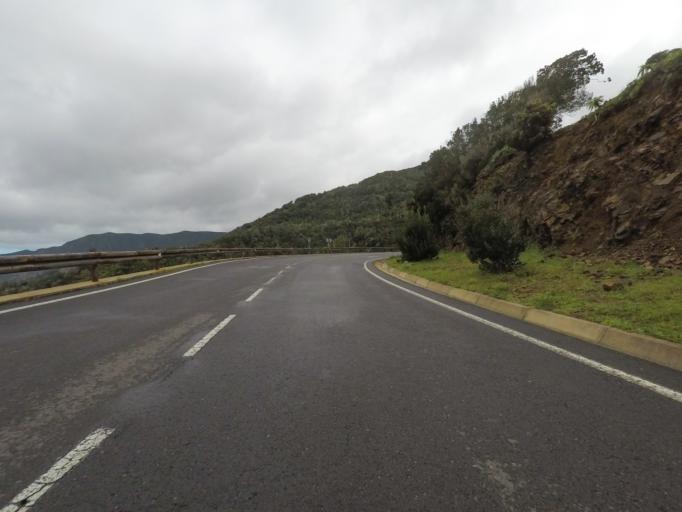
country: ES
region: Canary Islands
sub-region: Provincia de Santa Cruz de Tenerife
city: Vallehermosa
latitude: 28.1570
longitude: -17.2877
